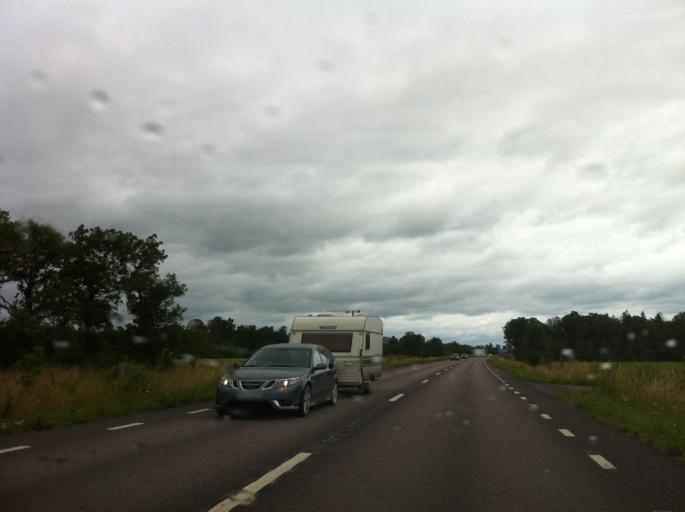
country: SE
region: Kalmar
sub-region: Borgholms Kommun
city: Borgholm
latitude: 57.1033
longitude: 16.9373
